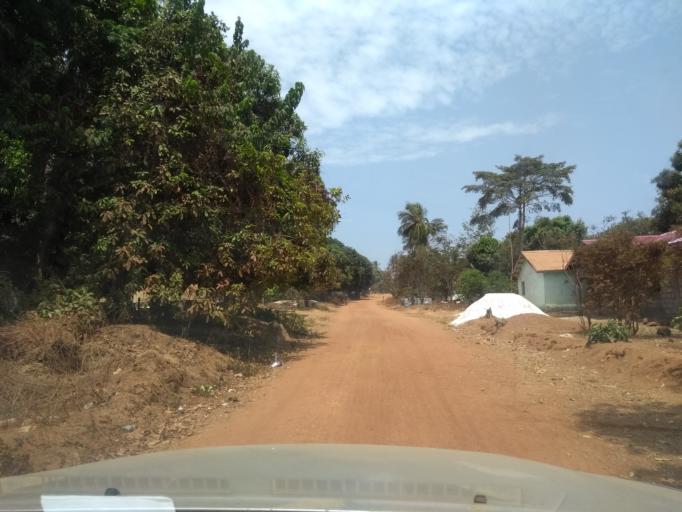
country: GN
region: Kindia
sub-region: Prefecture de Dubreka
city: Dubreka
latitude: 9.7863
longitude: -13.5451
